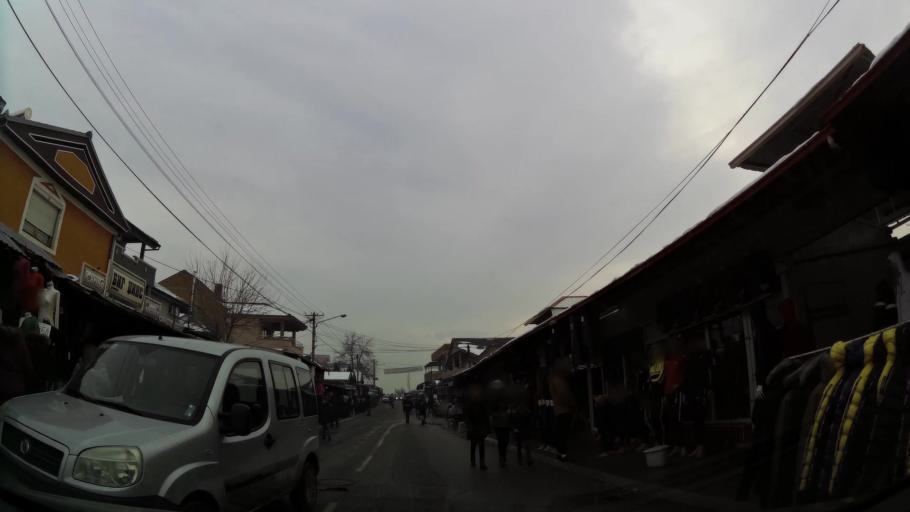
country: MK
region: Suto Orizari
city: Suto Orizare
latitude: 42.0400
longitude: 21.4243
